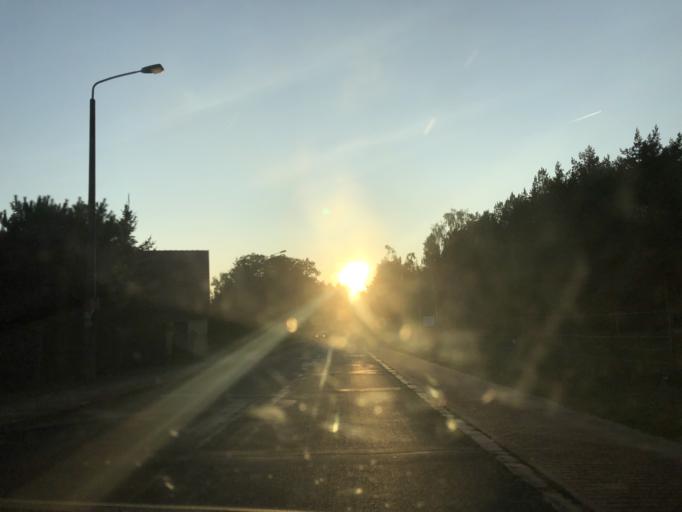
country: DE
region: Brandenburg
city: Mullrose
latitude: 52.2463
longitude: 14.4741
